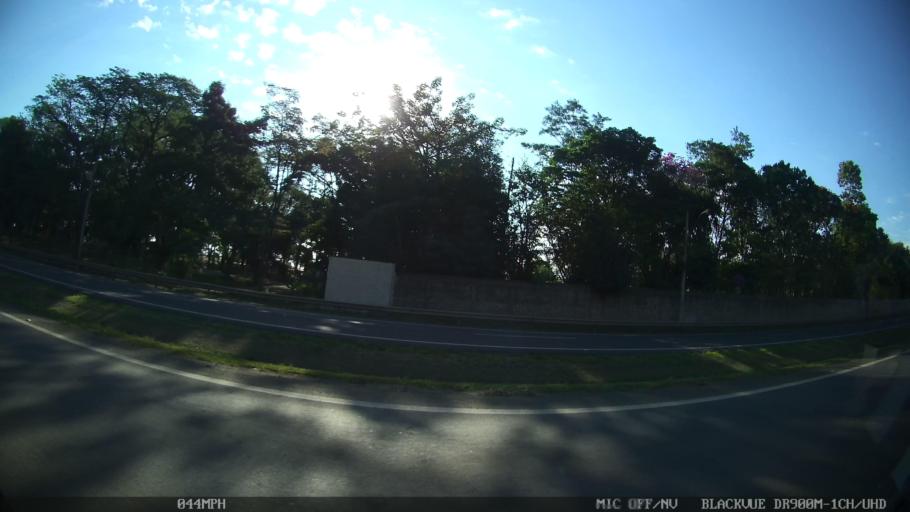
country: BR
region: Sao Paulo
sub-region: Piracicaba
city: Piracicaba
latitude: -22.6962
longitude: -47.6513
